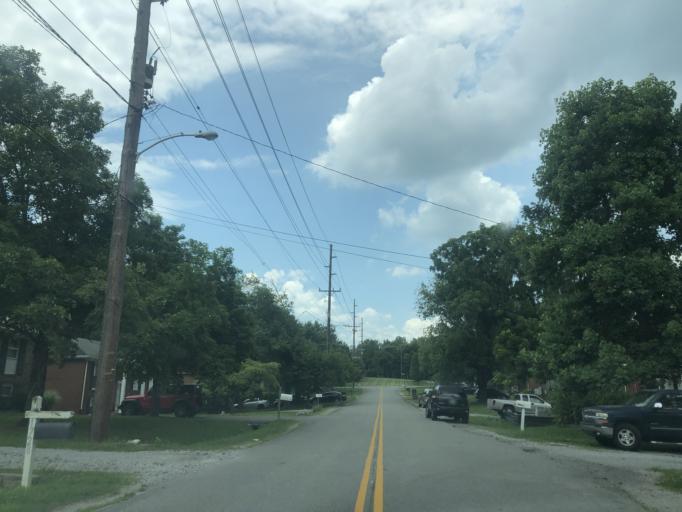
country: US
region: Tennessee
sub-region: Davidson County
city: Oak Hill
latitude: 36.0994
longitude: -86.6661
